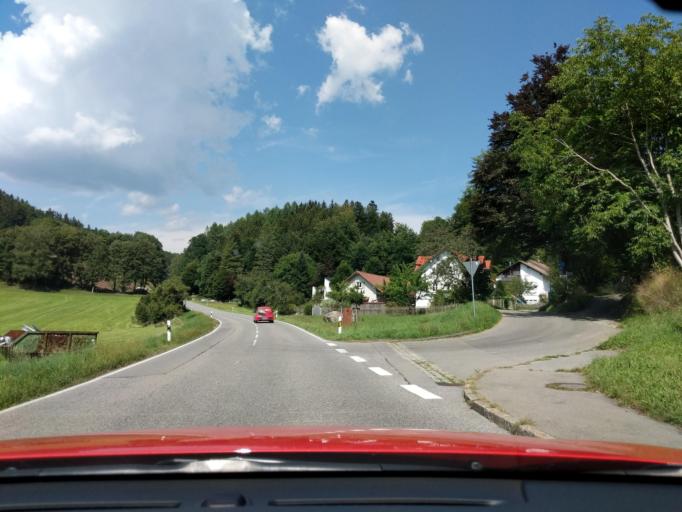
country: DE
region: Baden-Wuerttemberg
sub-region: Tuebingen Region
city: Vogt
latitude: 47.7515
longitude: 9.8054
